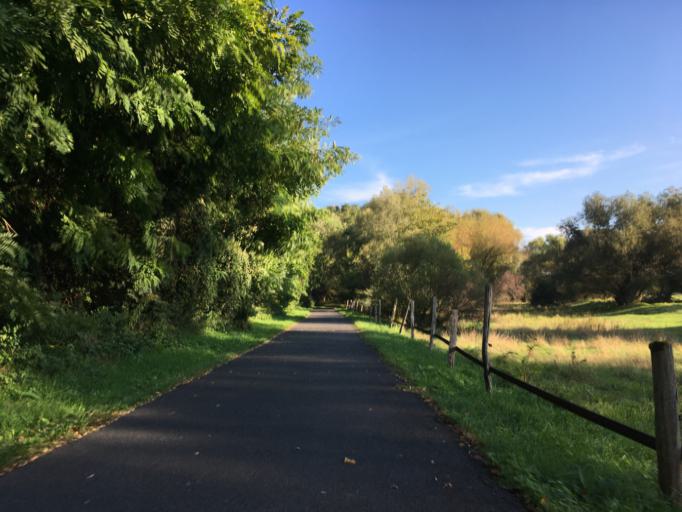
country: DE
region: Brandenburg
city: Lebus
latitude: 52.4346
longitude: 14.5444
